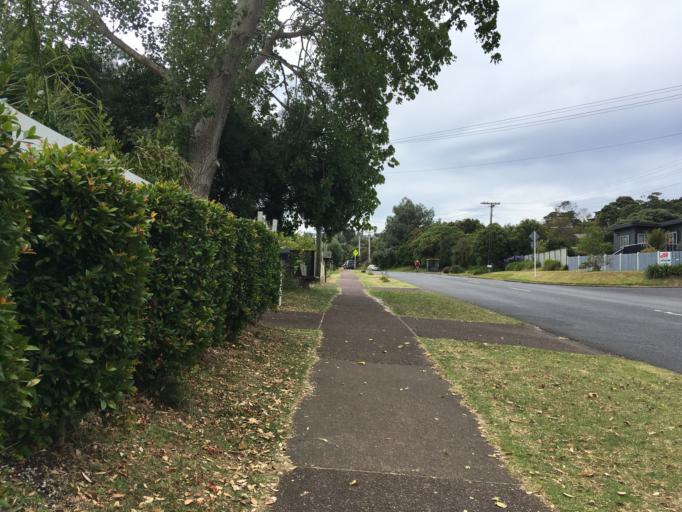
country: NZ
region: Auckland
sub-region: Auckland
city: Pakuranga
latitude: -36.7919
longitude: 175.0230
